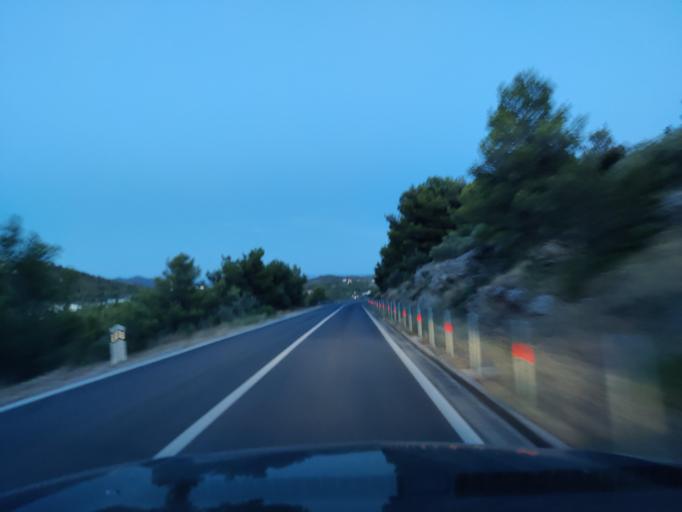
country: HR
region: Sibensko-Kniniska
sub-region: Grad Sibenik
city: Tisno
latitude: 43.7951
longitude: 15.6227
